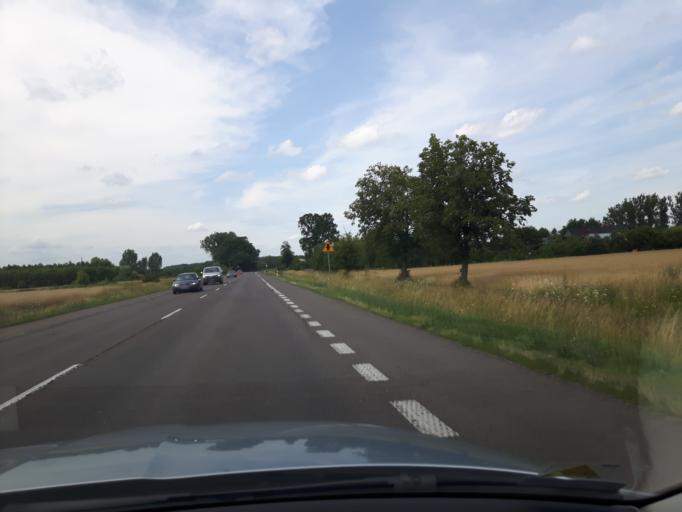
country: PL
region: Masovian Voivodeship
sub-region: Powiat ciechanowski
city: Glinojeck
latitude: 52.7662
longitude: 20.2994
